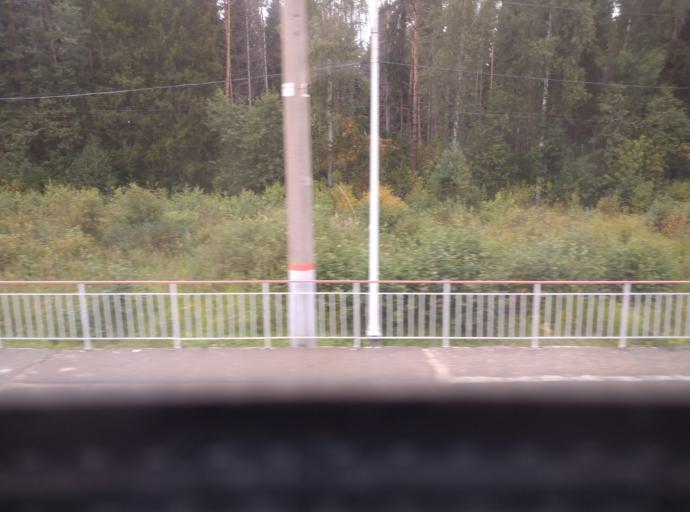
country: RU
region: Kostroma
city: Nerekhta
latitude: 57.4446
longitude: 40.4235
